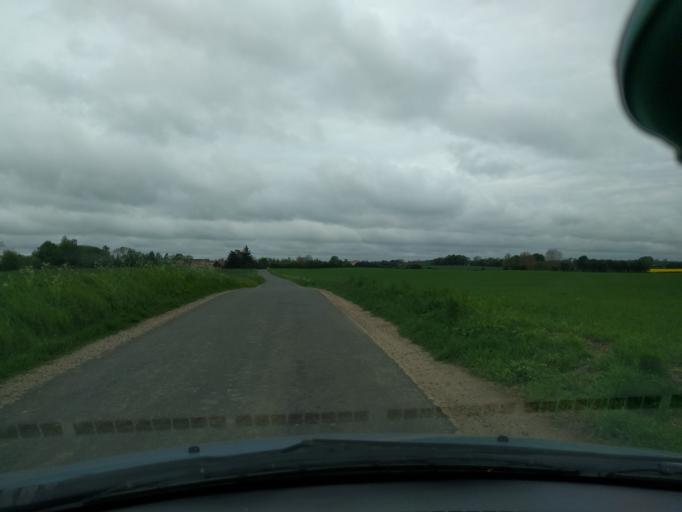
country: DK
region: South Denmark
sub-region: Nyborg Kommune
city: Ullerslev
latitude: 55.3681
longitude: 10.6408
